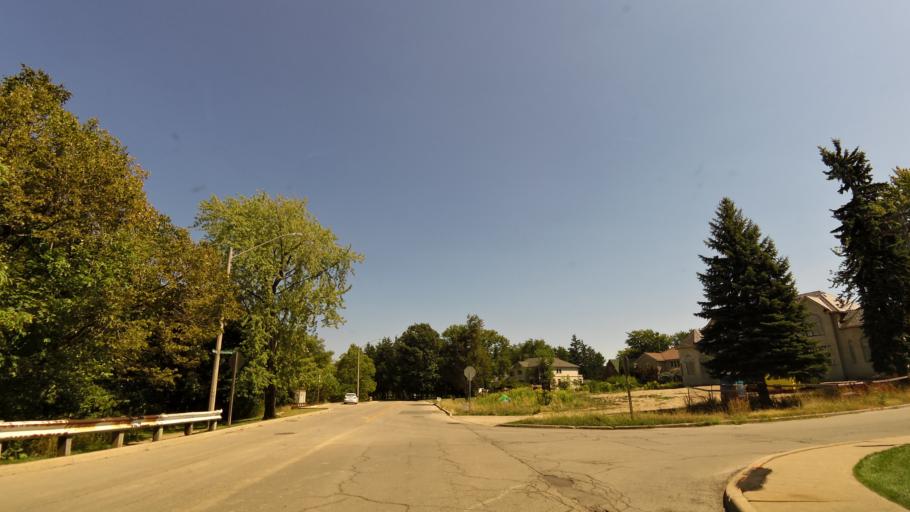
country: CA
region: Ontario
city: Ancaster
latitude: 43.2455
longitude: -79.9228
